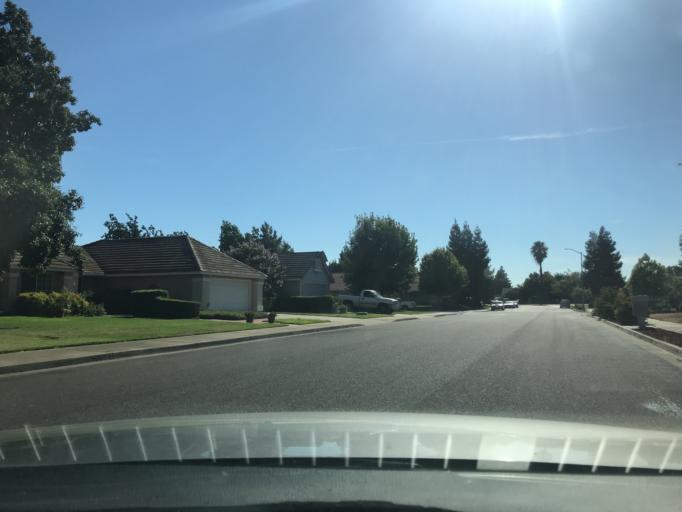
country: US
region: California
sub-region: Merced County
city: Atwater
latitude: 37.3487
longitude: -120.5849
